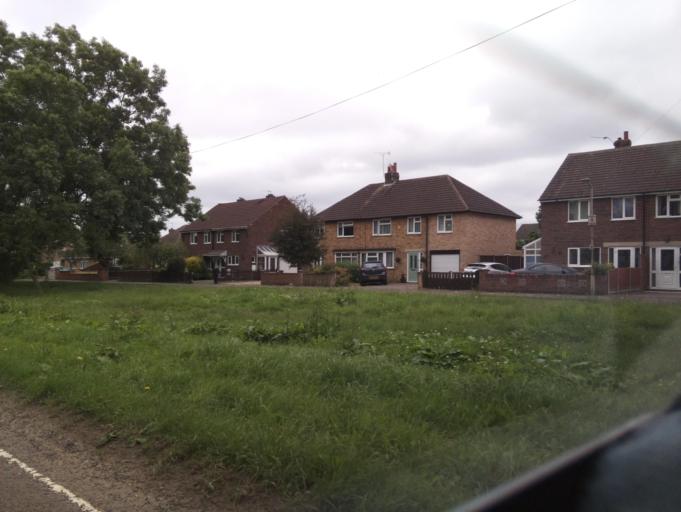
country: GB
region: England
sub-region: Leicestershire
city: Asfordby
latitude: 52.7648
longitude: -0.9597
